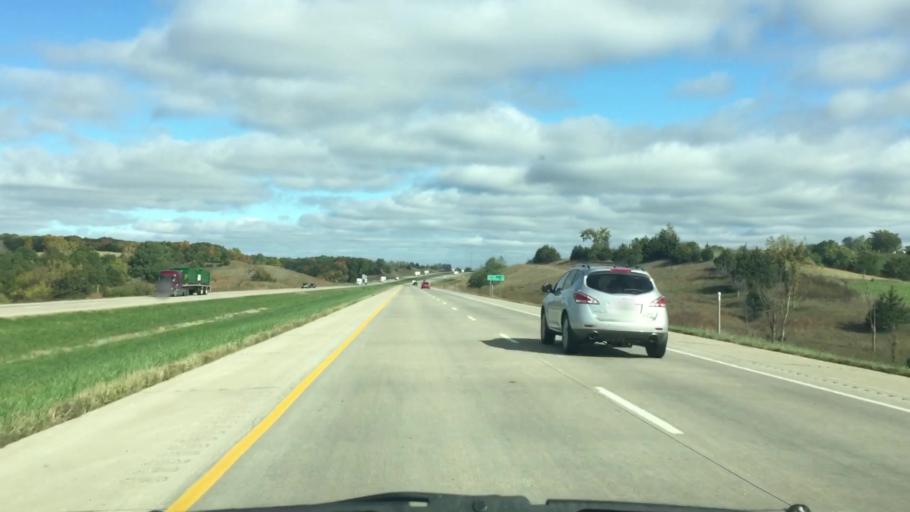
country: US
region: Iowa
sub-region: Decatur County
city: Leon
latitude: 40.8825
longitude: -93.8011
